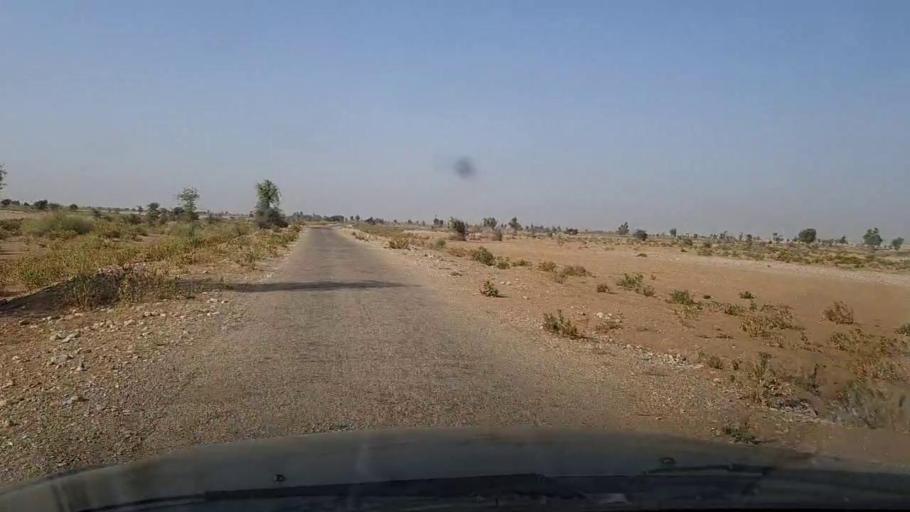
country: PK
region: Sindh
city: Sann
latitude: 25.9702
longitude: 68.0527
